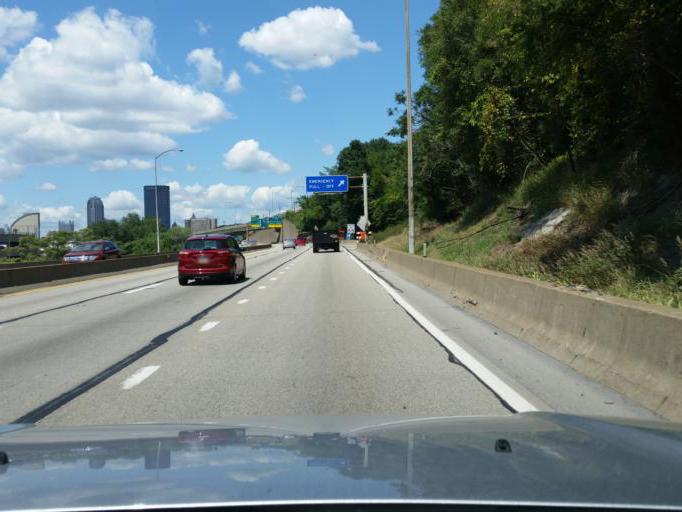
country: US
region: Pennsylvania
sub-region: Allegheny County
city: Bloomfield
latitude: 40.4346
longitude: -79.9652
